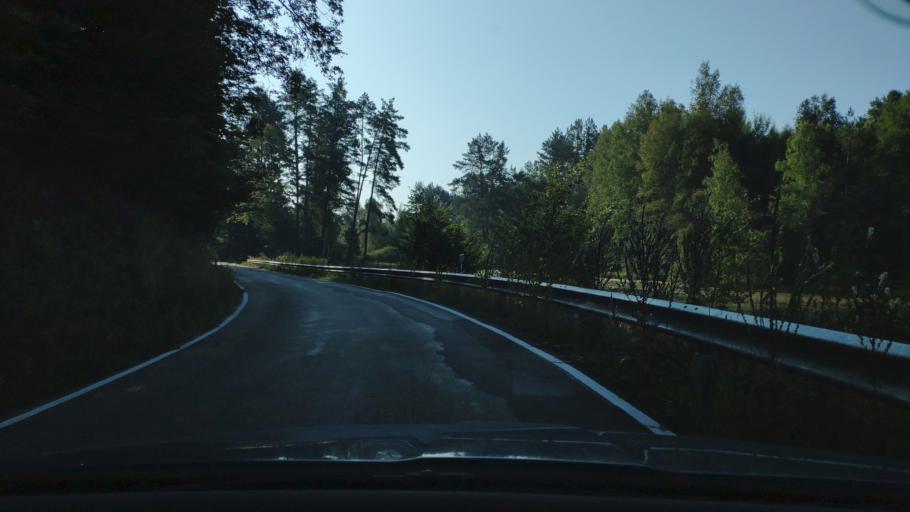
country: DE
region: Rheinland-Pfalz
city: Ludwigswinkel
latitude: 49.0910
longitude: 7.6419
